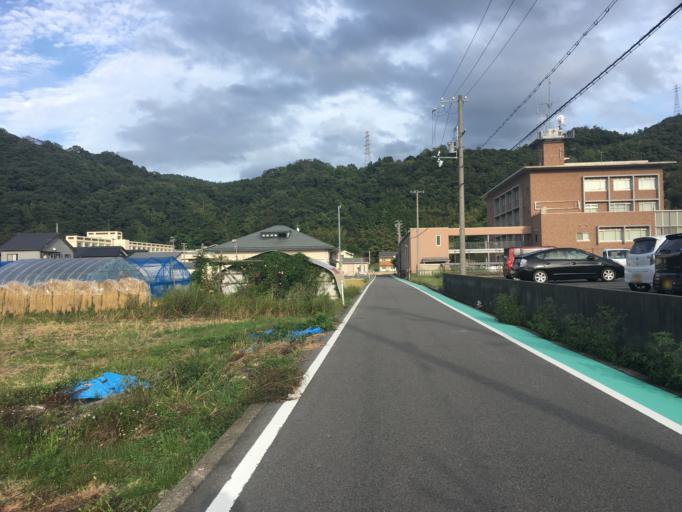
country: JP
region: Hyogo
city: Toyooka
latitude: 35.6325
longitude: 134.6279
